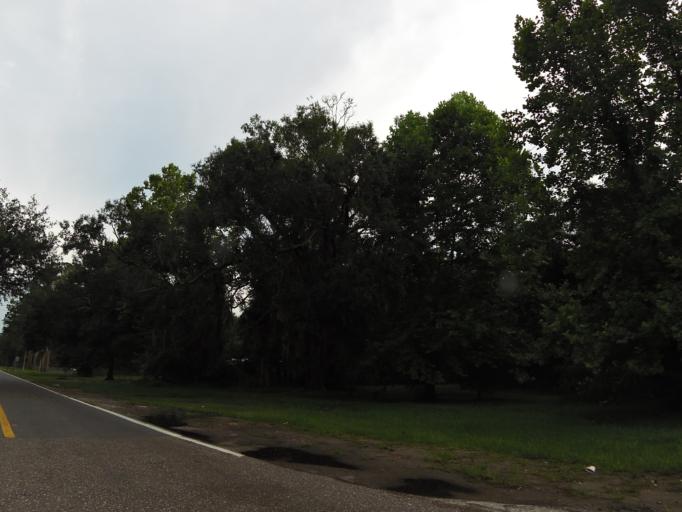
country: US
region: Florida
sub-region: Nassau County
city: Nassau Village-Ratliff
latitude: 30.4158
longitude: -81.7602
